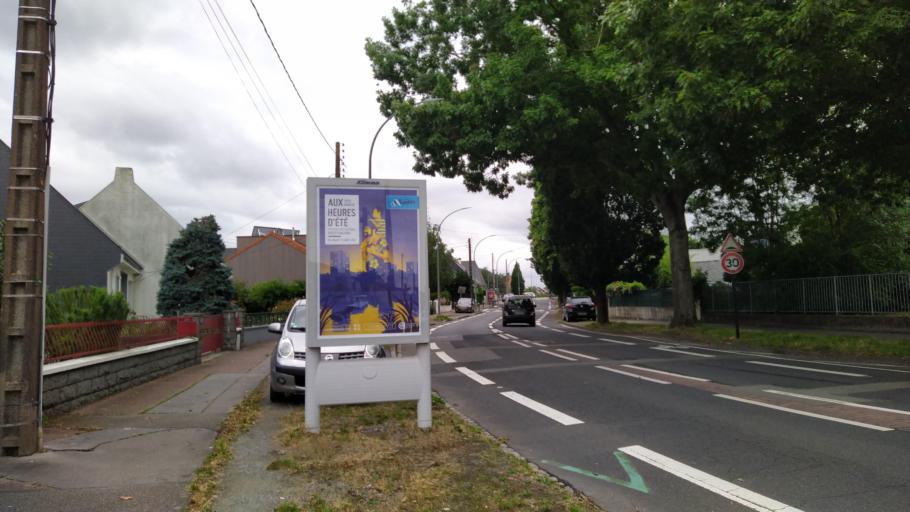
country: FR
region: Pays de la Loire
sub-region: Departement de la Loire-Atlantique
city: Saint-Sebastien-sur-Loire
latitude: 47.2340
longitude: -1.5097
